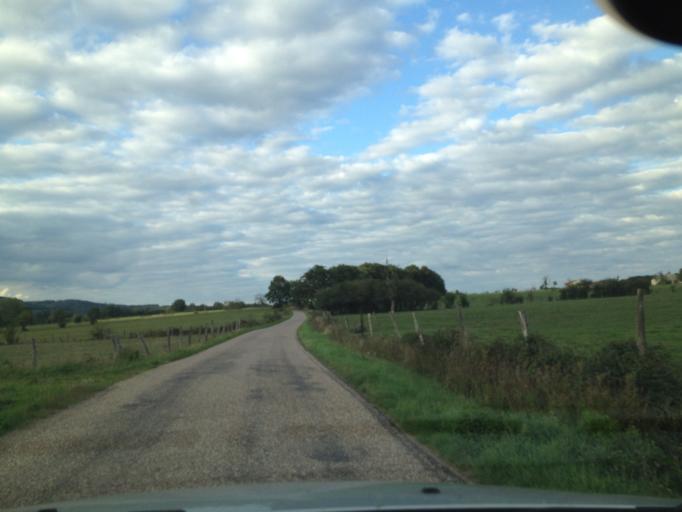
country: FR
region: Lorraine
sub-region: Departement des Vosges
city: Bains-les-Bains
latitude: 47.9832
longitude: 6.2073
